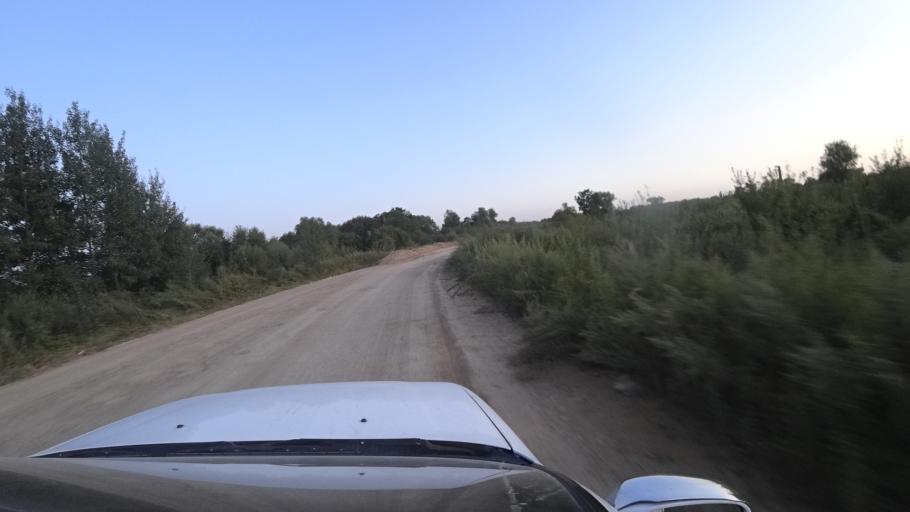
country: RU
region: Primorskiy
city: Dal'nerechensk
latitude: 45.9415
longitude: 133.7612
